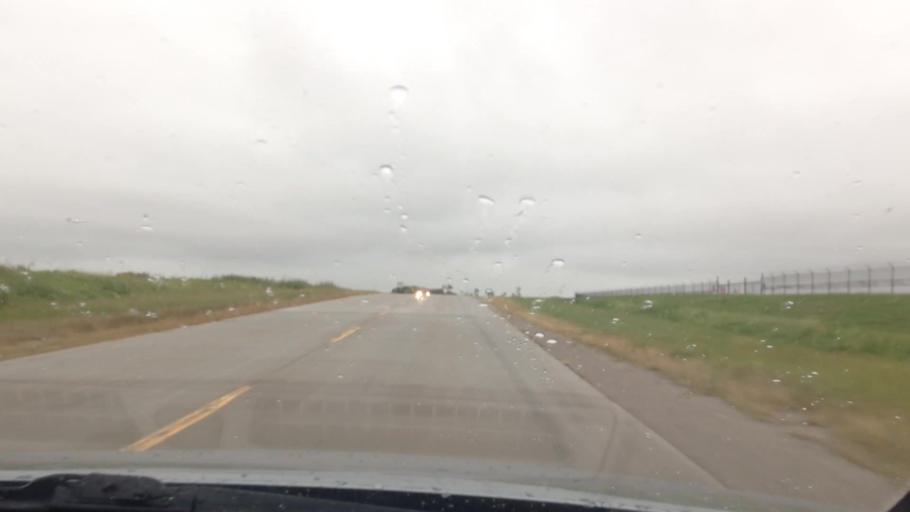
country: US
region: Missouri
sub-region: Platte County
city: Platte City
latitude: 39.3318
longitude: -94.7188
